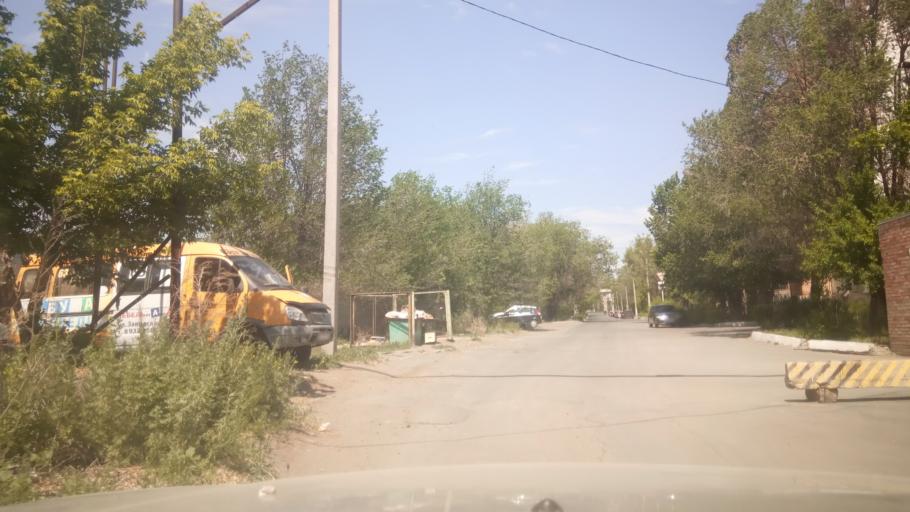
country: RU
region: Orenburg
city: Novotroitsk
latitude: 51.1934
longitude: 58.3013
